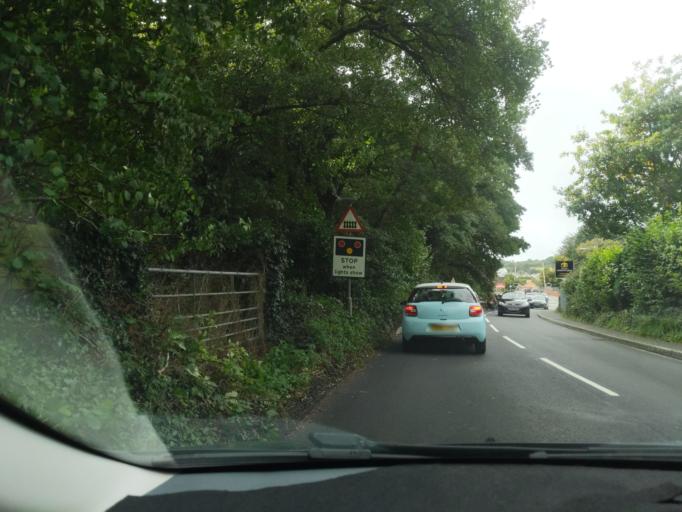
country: GB
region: England
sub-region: Cornwall
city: Par
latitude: 50.3579
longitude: -4.7090
